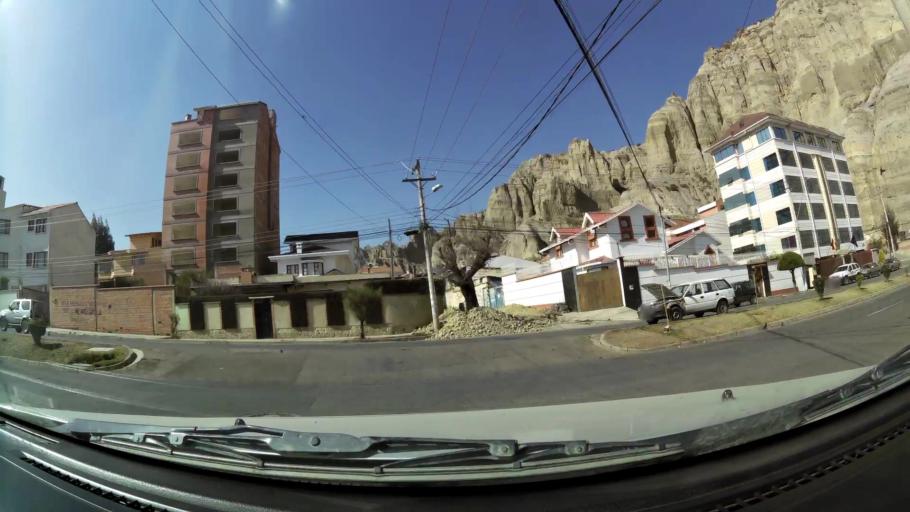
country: BO
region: La Paz
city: La Paz
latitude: -16.5312
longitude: -68.0694
